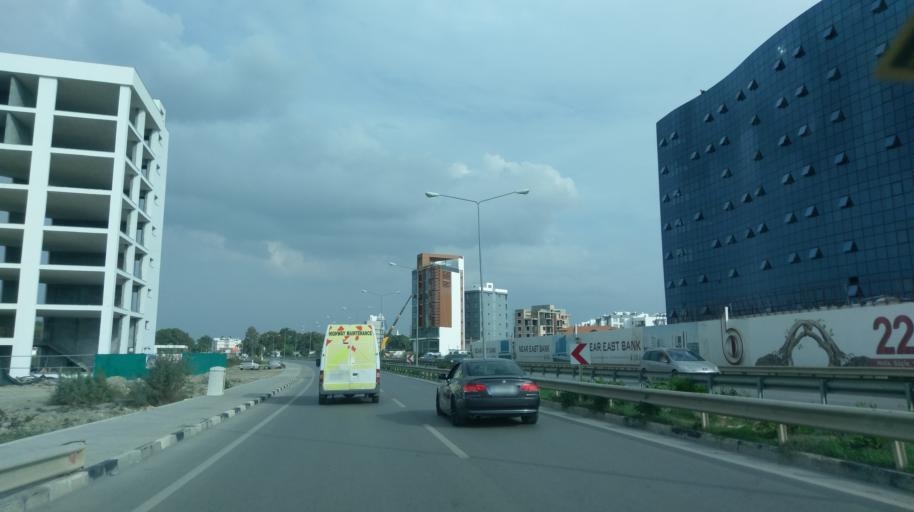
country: CY
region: Lefkosia
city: Nicosia
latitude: 35.1898
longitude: 33.3418
